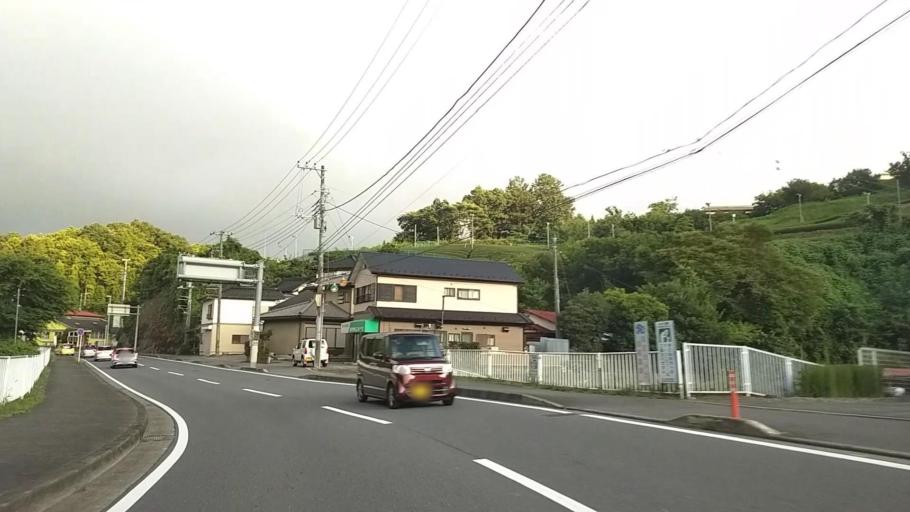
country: JP
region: Kanagawa
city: Atsugi
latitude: 35.4730
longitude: 139.2852
